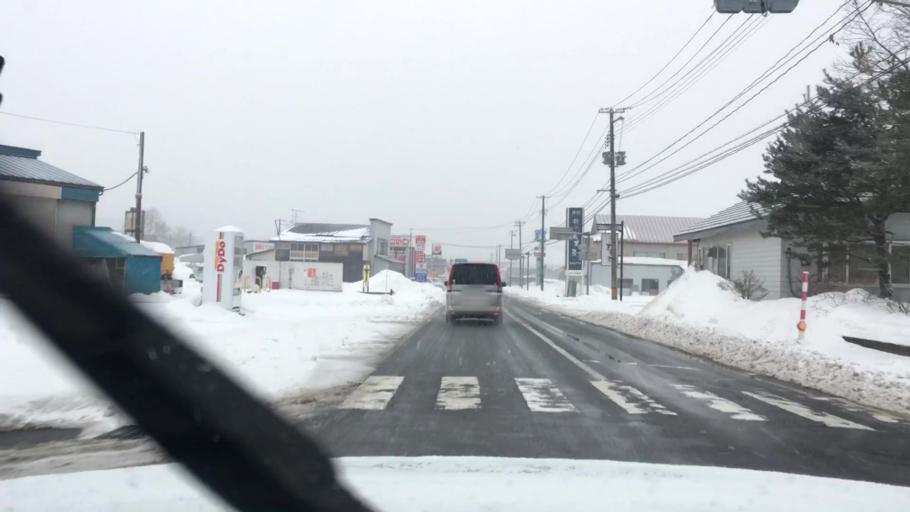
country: JP
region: Iwate
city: Ichinohe
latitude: 40.1052
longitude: 141.0499
